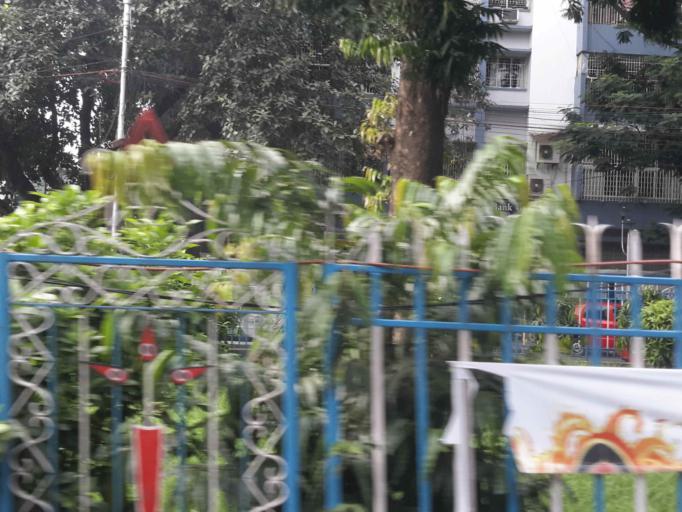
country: IN
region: West Bengal
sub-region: Kolkata
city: Kolkata
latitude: 22.5134
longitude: 88.3563
